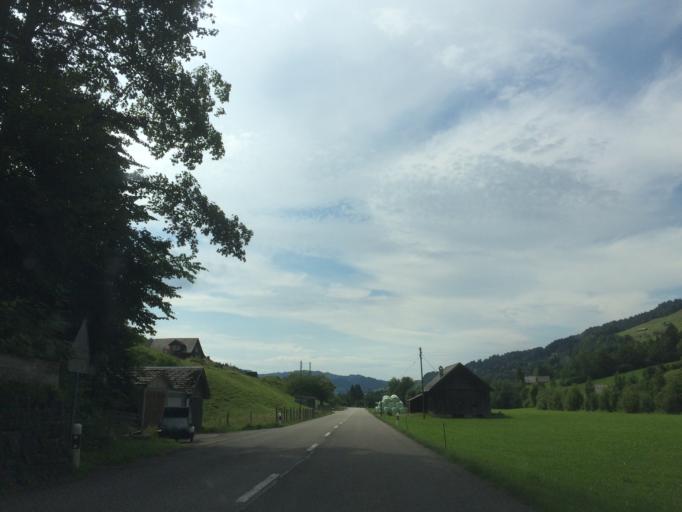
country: CH
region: Saint Gallen
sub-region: Wahlkreis Toggenburg
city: Krummenau
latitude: 47.2453
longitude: 9.2482
